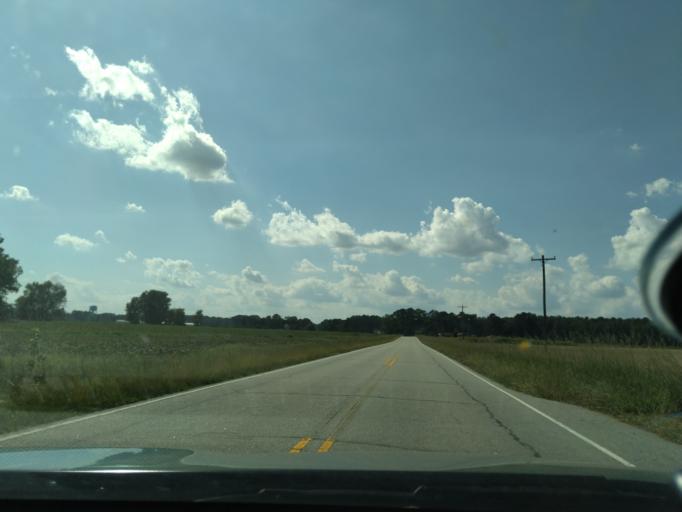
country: US
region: North Carolina
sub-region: Martin County
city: Robersonville
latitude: 35.8286
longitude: -77.2262
